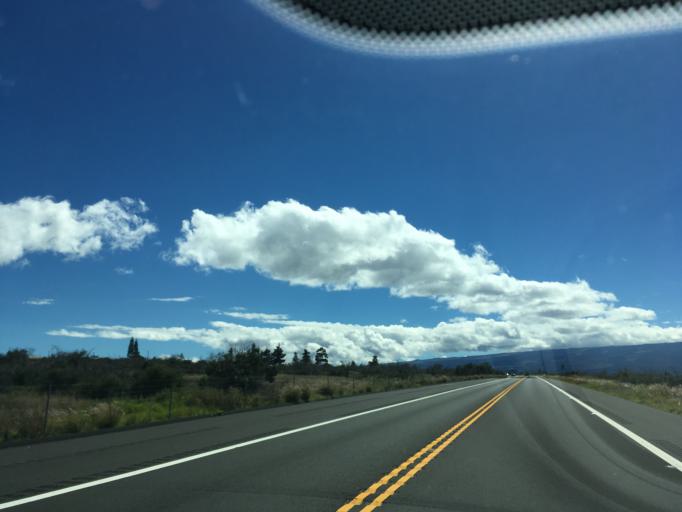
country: US
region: Hawaii
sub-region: Hawaii County
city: Waimea
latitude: 19.7541
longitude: -155.5298
